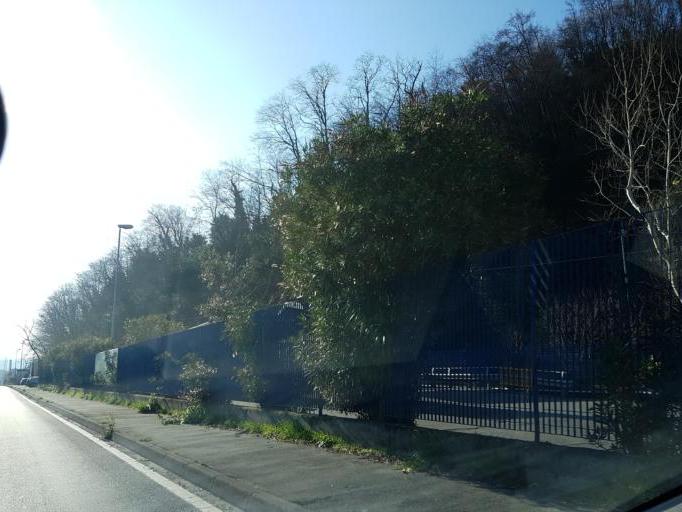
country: IT
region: Liguria
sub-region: Provincia di Genova
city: Santa Marta
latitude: 44.4850
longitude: 8.8981
